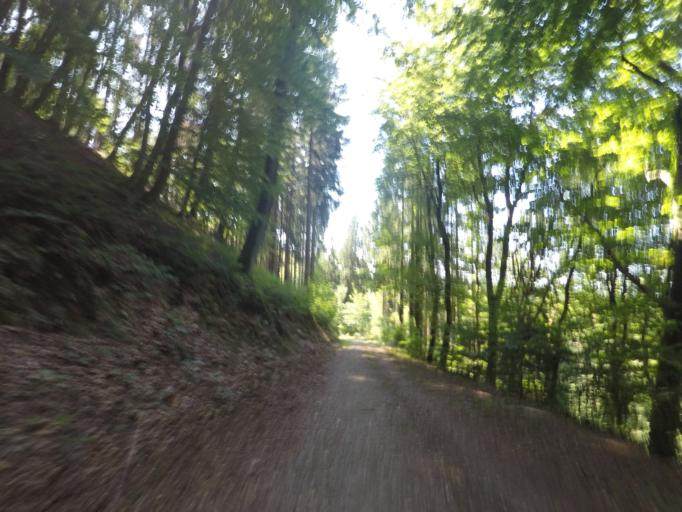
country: LU
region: Luxembourg
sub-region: Canton de Capellen
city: Kopstal
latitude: 49.6555
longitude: 6.0688
